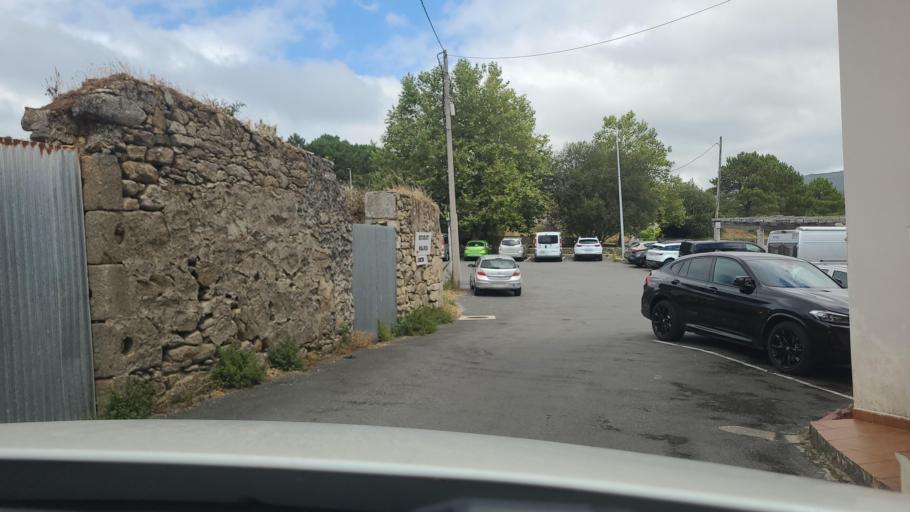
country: ES
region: Galicia
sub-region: Provincia da Coruna
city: Fisterra
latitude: 42.9148
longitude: -9.2660
